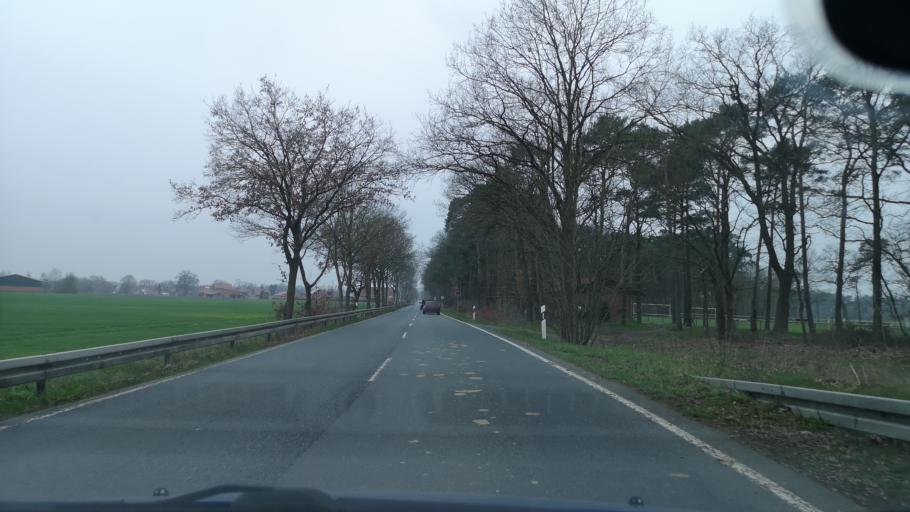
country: DE
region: Lower Saxony
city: Neustadt am Rubenberge
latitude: 52.5755
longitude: 9.5120
